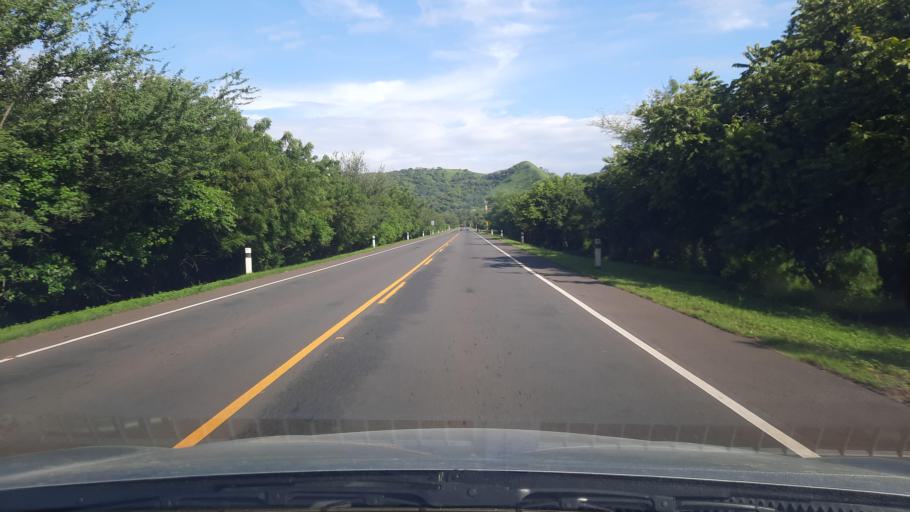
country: NI
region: Leon
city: Telica
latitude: 12.7052
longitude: -86.8710
